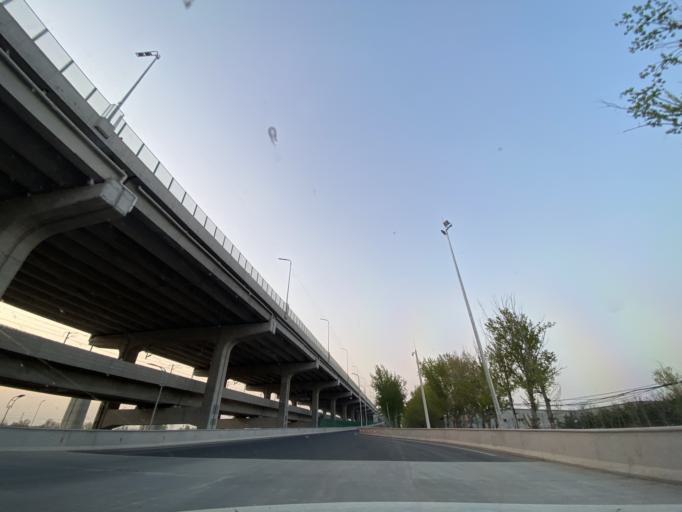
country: CN
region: Beijing
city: Weishanzhuang
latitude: 39.6164
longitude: 116.3790
